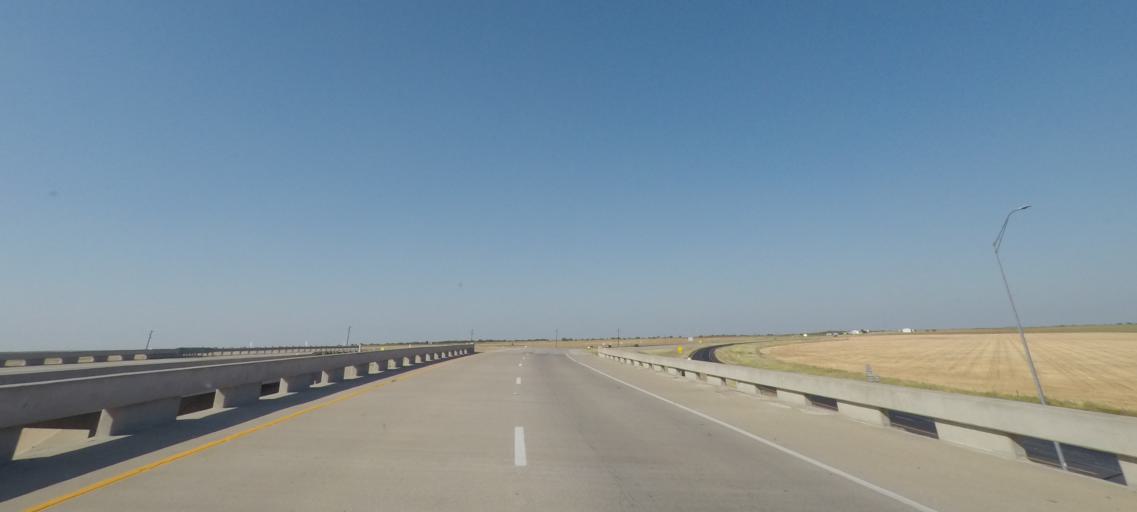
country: US
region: Texas
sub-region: Baylor County
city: Seymour
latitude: 33.6152
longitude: -99.2428
